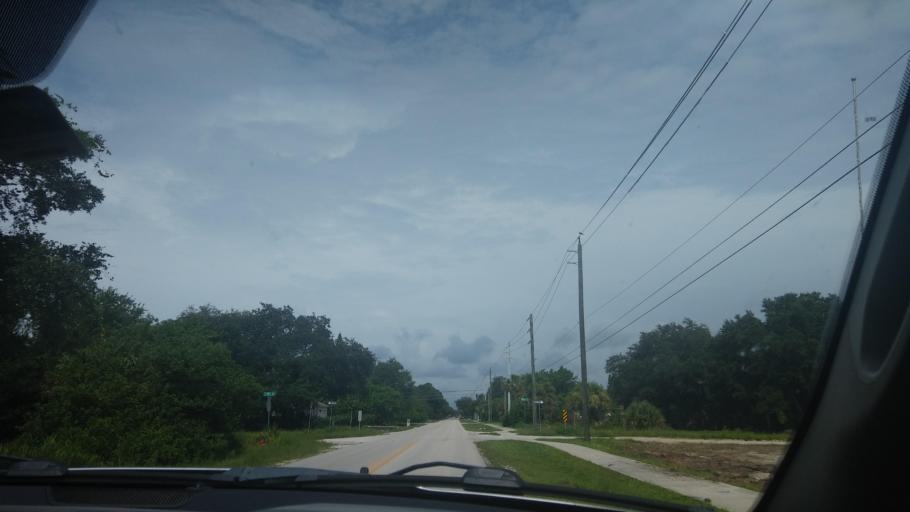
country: US
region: Florida
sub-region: Indian River County
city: Fellsmere
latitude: 27.7527
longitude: -80.5272
